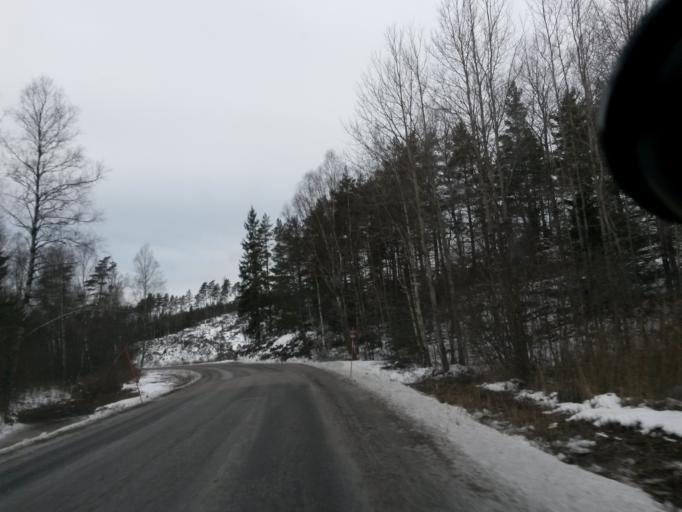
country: SE
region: Vaestra Goetaland
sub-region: Vargarda Kommun
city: Jonstorp
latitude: 57.9477
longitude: 12.6603
